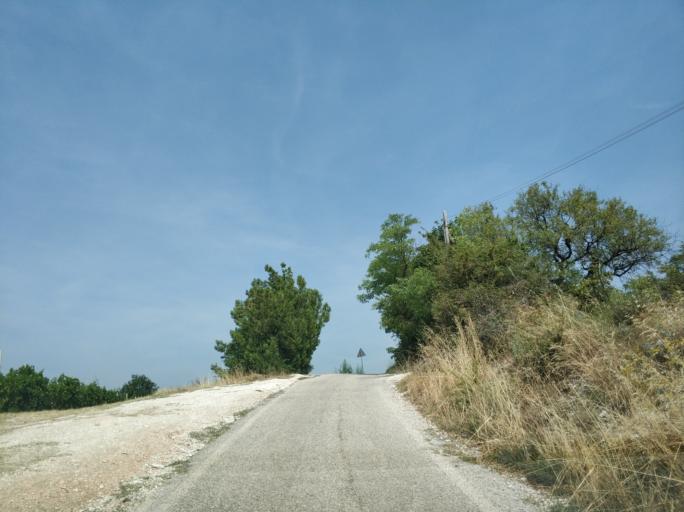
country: IT
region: Veneto
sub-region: Provincia di Padova
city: Arqua Petrarca
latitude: 45.2780
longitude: 11.7059
